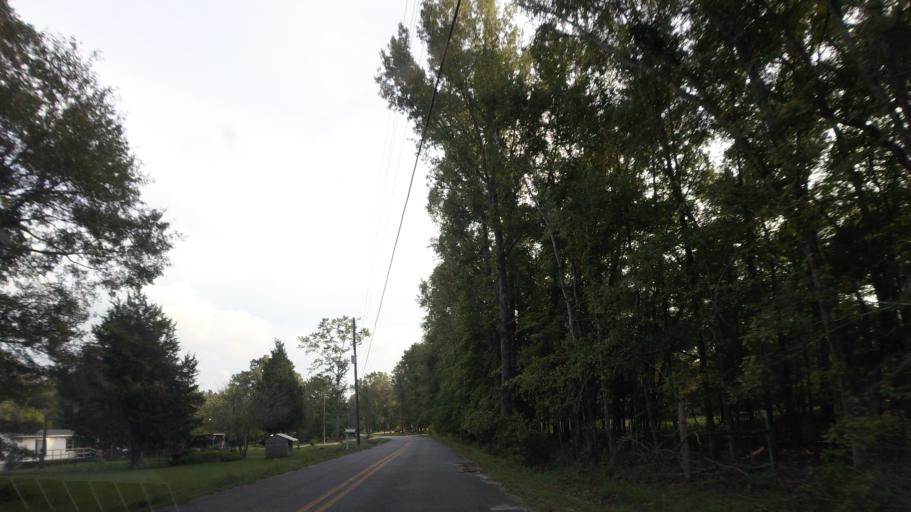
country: US
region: Georgia
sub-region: Wilkinson County
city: Gordon
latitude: 32.8300
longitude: -83.3911
